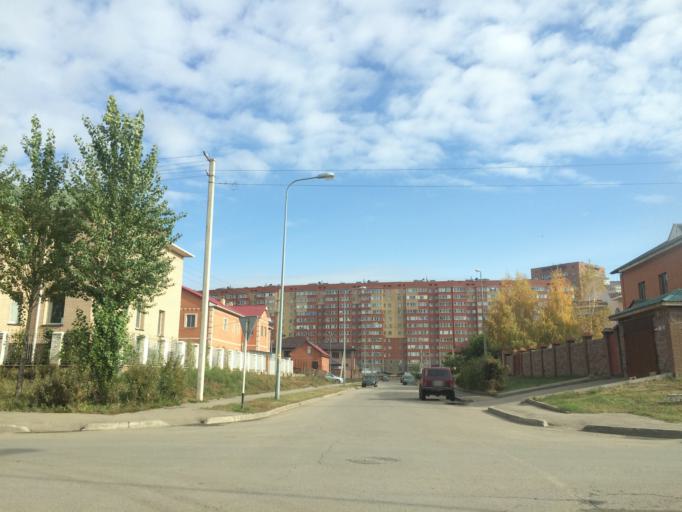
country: KZ
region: Astana Qalasy
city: Astana
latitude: 51.1773
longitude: 71.3725
